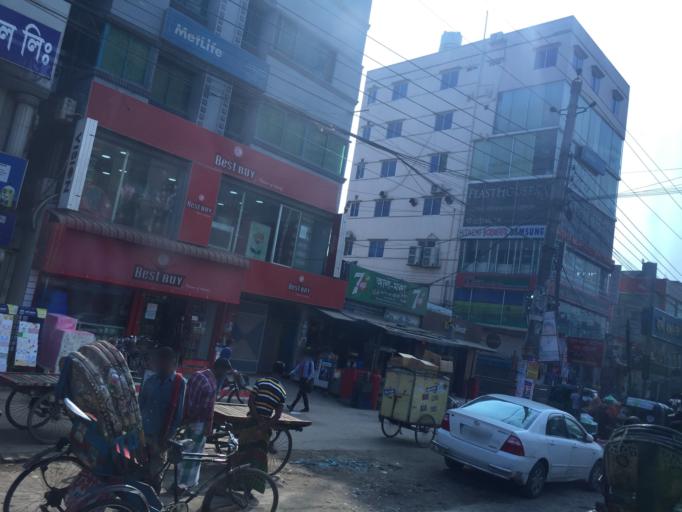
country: BD
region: Dhaka
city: Paltan
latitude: 23.7735
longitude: 90.4259
